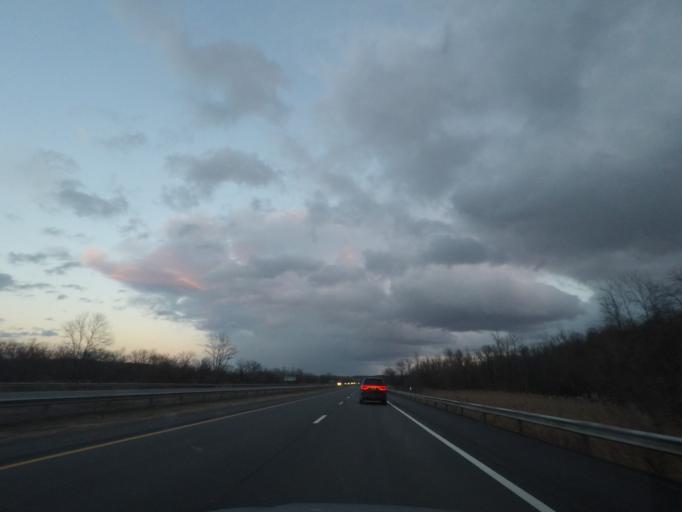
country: US
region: New York
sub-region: Montgomery County
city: Fonda
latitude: 42.9379
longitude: -74.3336
